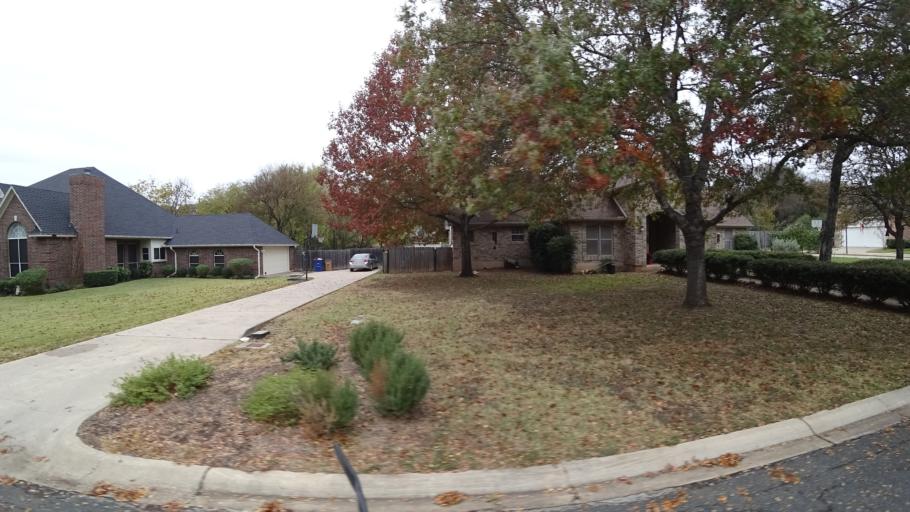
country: US
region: Texas
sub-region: Williamson County
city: Jollyville
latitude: 30.3734
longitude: -97.7856
